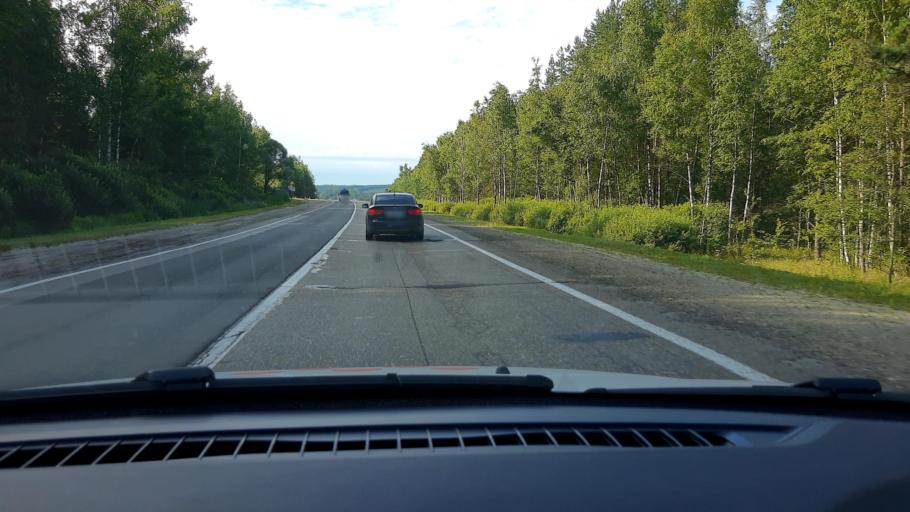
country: RU
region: Nizjnij Novgorod
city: Surovatikha
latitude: 55.6202
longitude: 43.9847
